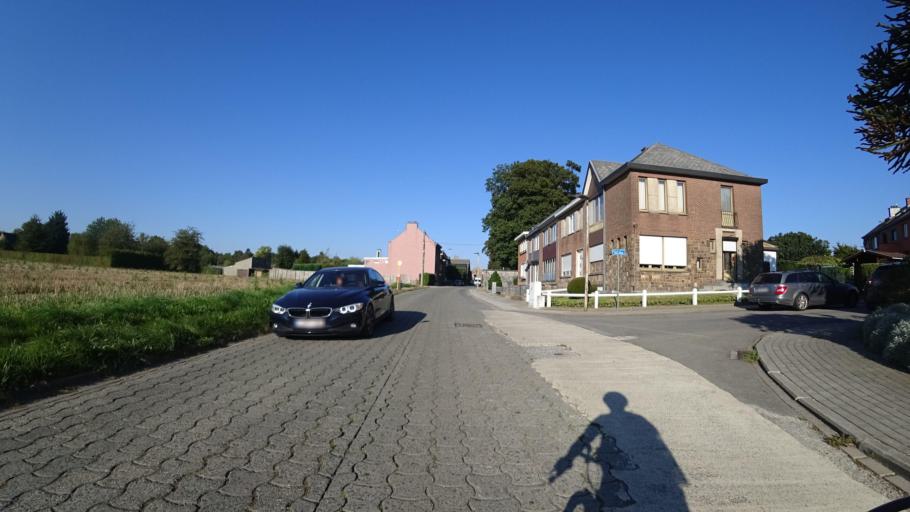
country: BE
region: Wallonia
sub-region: Province de Namur
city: Namur
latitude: 50.4741
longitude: 4.8297
